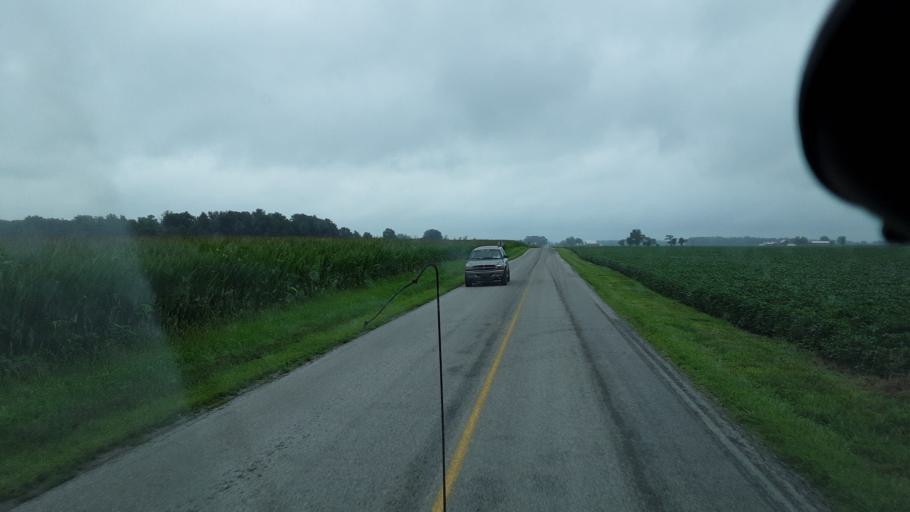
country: US
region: Indiana
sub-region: Wells County
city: Ossian
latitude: 40.8875
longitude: -85.1094
